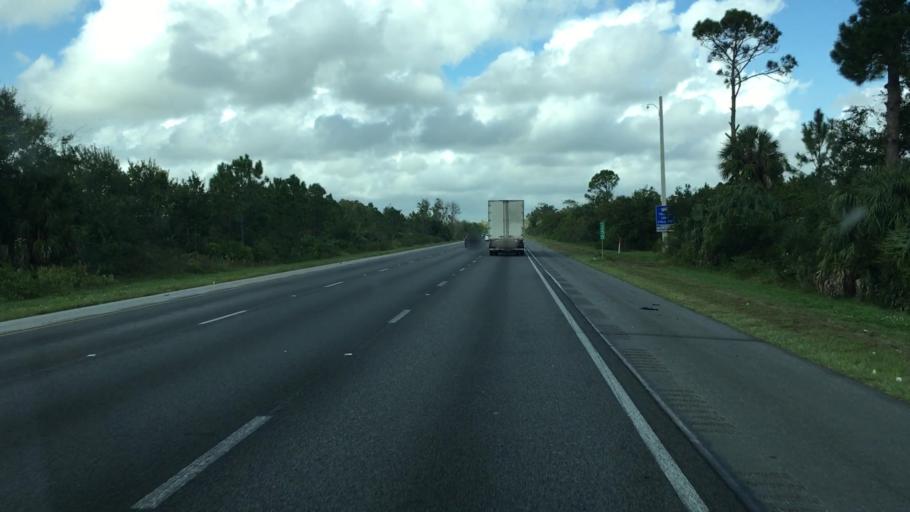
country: US
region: Florida
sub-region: Volusia County
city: Glencoe
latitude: 29.0281
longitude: -80.9976
